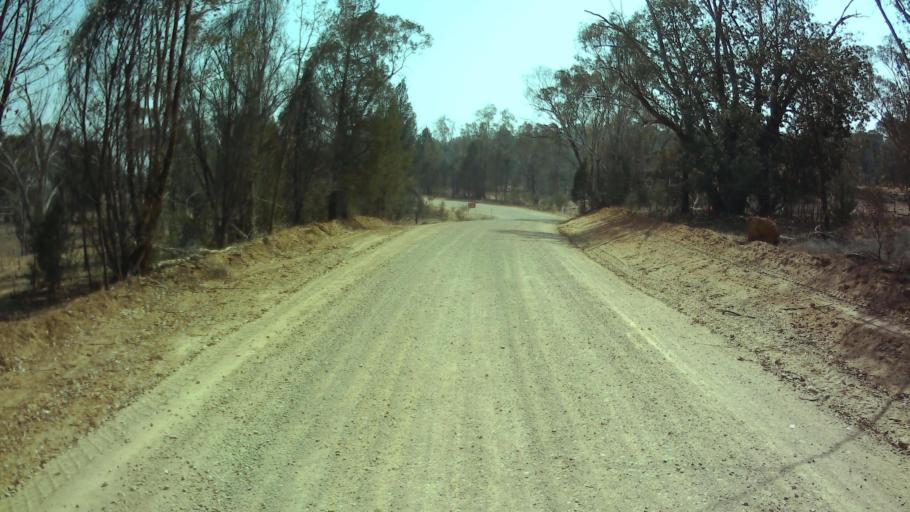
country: AU
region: New South Wales
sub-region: Weddin
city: Grenfell
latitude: -33.6625
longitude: 148.2746
